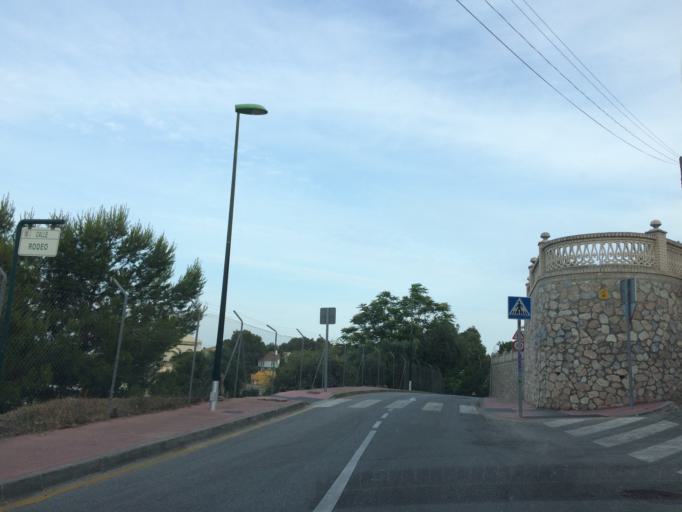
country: ES
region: Andalusia
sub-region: Provincia de Malaga
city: Malaga
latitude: 36.7270
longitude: -4.3855
